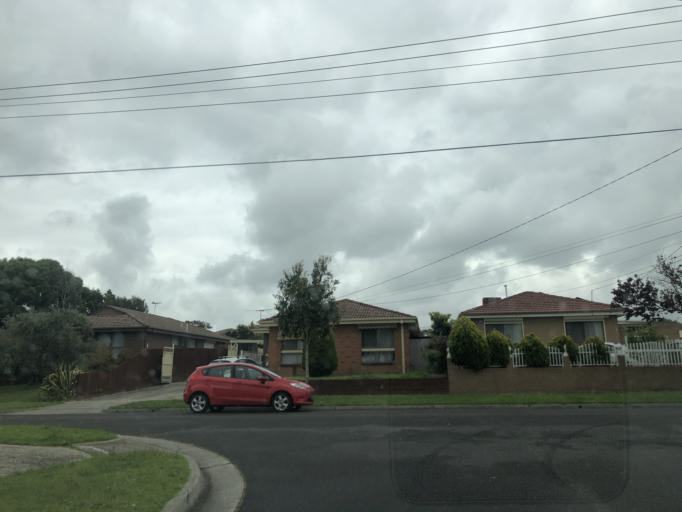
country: AU
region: Victoria
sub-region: Greater Dandenong
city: Dandenong North
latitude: -37.9607
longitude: 145.2119
